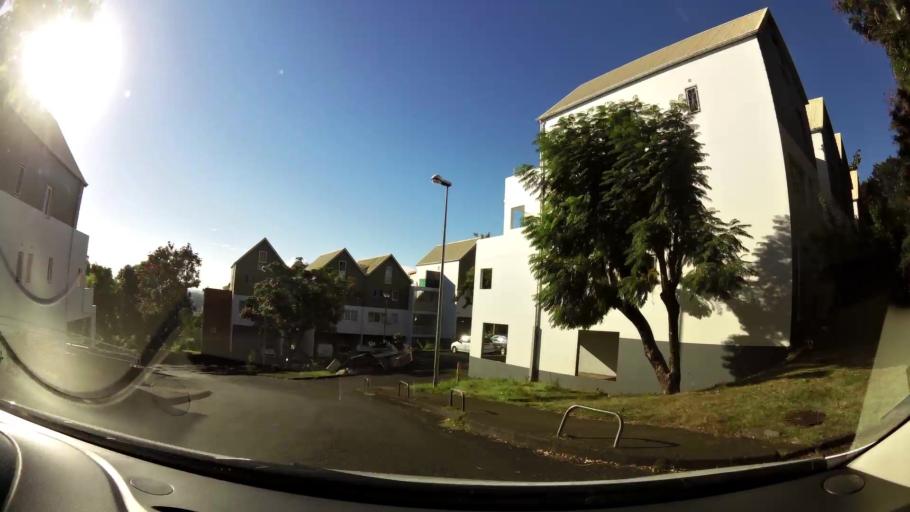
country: RE
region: Reunion
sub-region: Reunion
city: Saint-Denis
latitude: -20.8945
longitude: 55.4509
